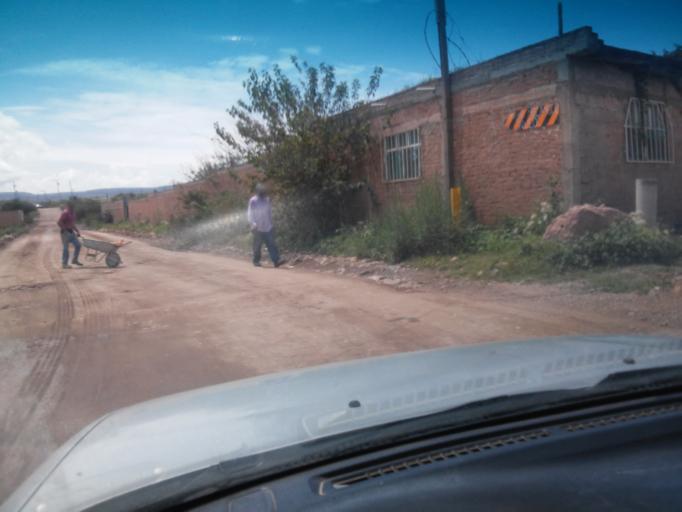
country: MX
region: Durango
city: Victoria de Durango
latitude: 23.9910
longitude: -104.7113
